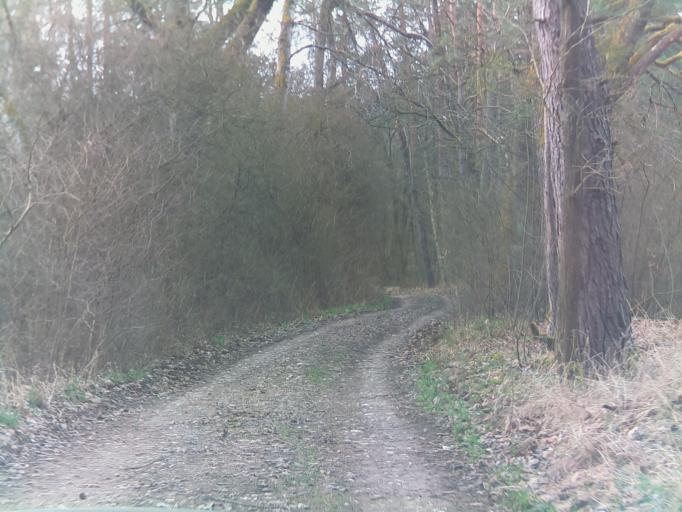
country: DE
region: Bavaria
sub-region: Upper Palatinate
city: Breitenbrunn
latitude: 49.3653
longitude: 12.0720
